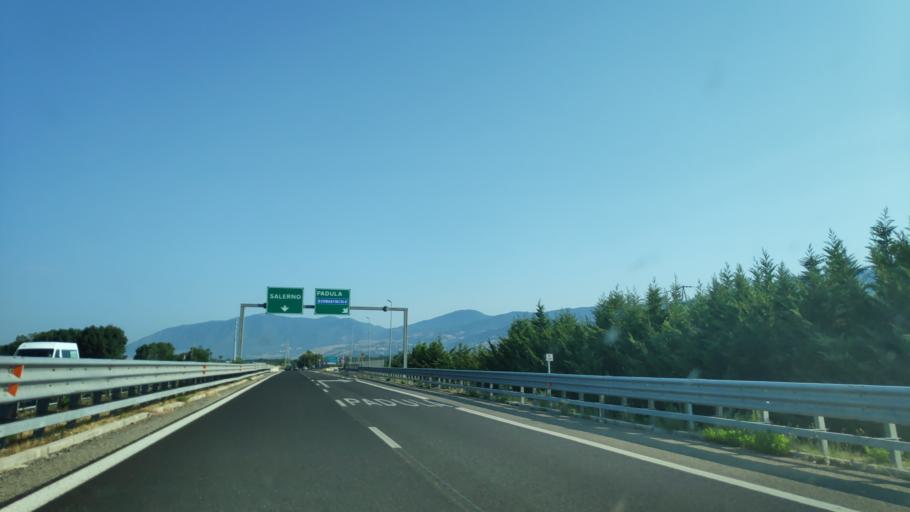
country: IT
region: Campania
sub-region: Provincia di Salerno
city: Buonabitacolo
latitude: 40.2956
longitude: 15.6481
